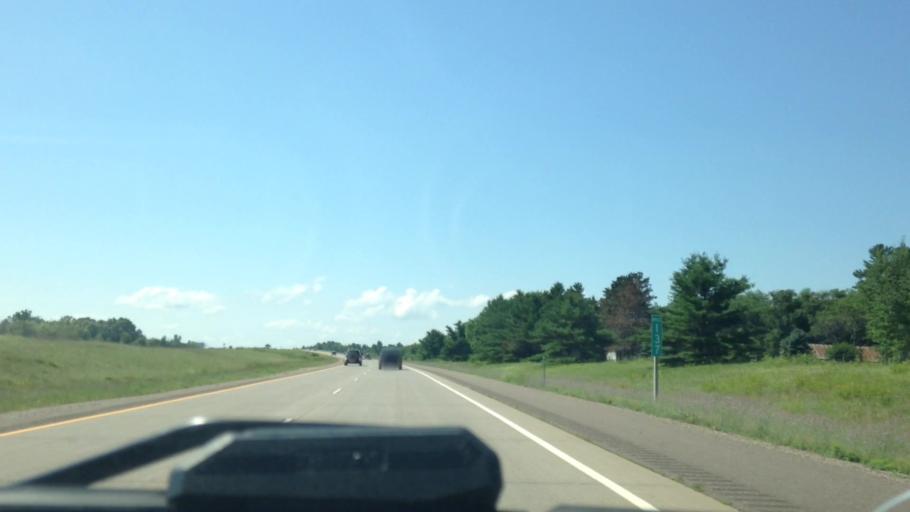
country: US
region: Wisconsin
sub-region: Barron County
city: Cameron
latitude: 45.4163
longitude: -91.7644
